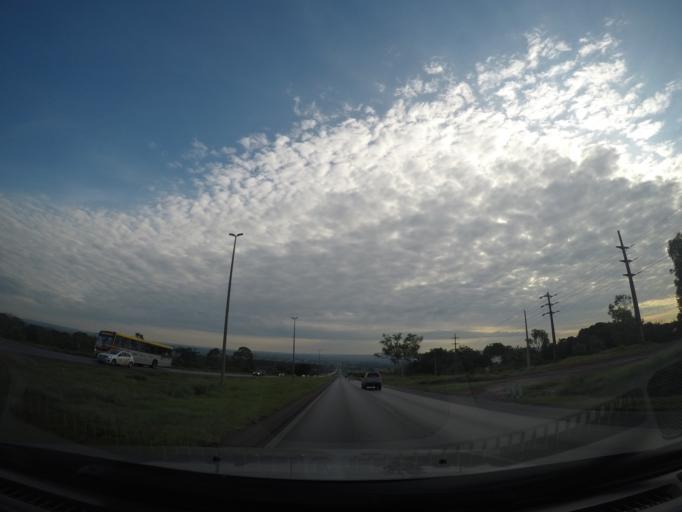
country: BR
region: Goias
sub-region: Planaltina
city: Planaltina
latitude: -15.6188
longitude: -47.7124
